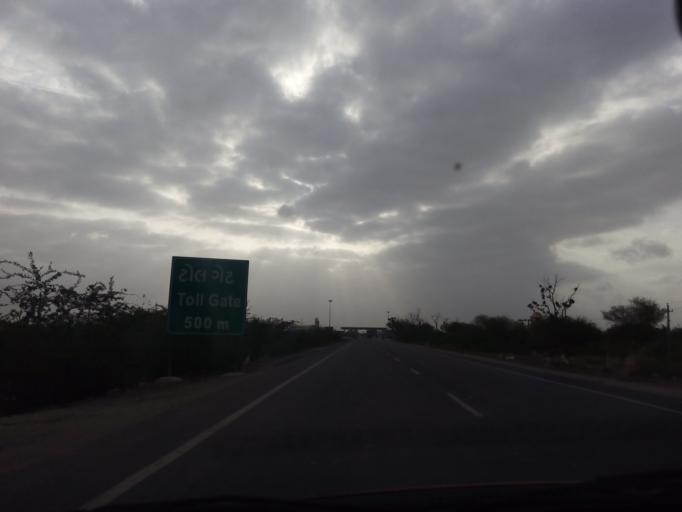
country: IN
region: Gujarat
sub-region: Kachchh
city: Bhuj
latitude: 23.2345
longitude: 69.7829
